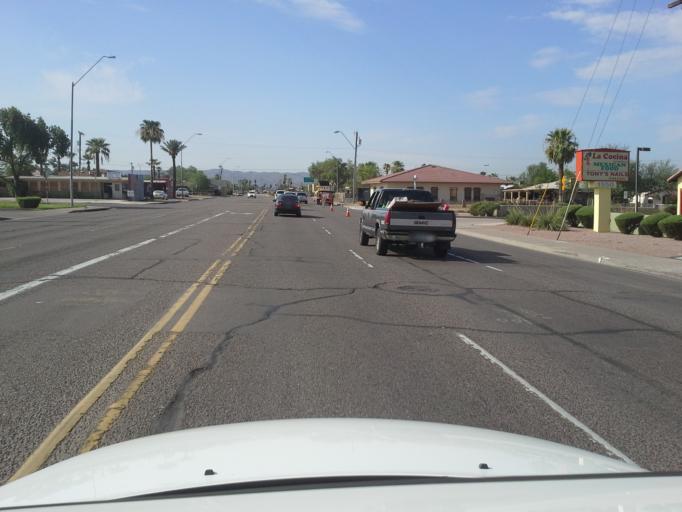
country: US
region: Arizona
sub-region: Maricopa County
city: Phoenix
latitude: 33.4654
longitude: -112.0477
